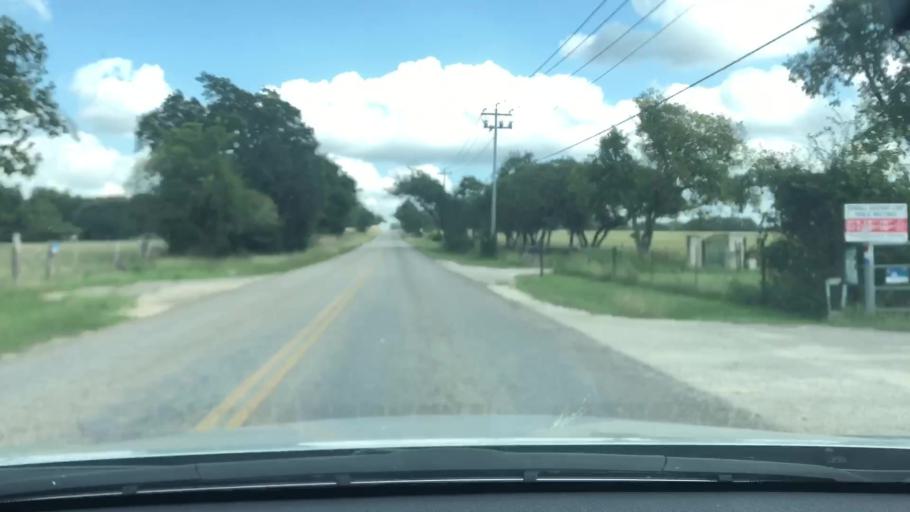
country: US
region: Texas
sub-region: Bexar County
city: Fair Oaks Ranch
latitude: 29.7860
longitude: -98.6663
